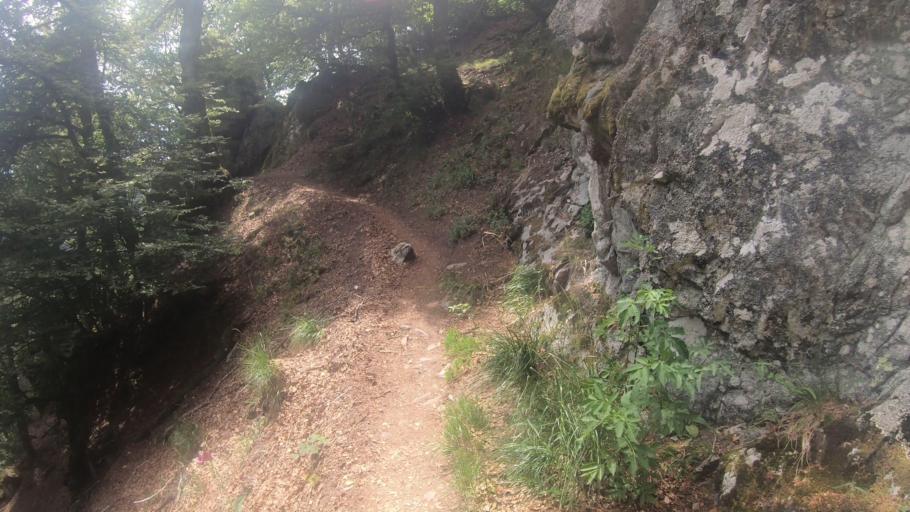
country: FR
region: Alsace
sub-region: Departement du Haut-Rhin
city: Metzeral
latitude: 48.0492
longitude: 7.0238
